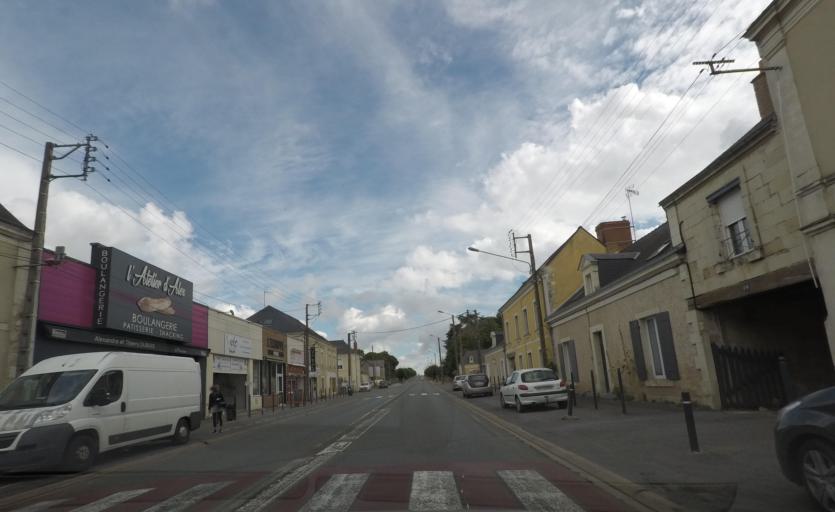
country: FR
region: Pays de la Loire
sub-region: Departement de Maine-et-Loire
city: Seiches-sur-le-Loir
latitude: 47.5732
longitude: -0.3552
